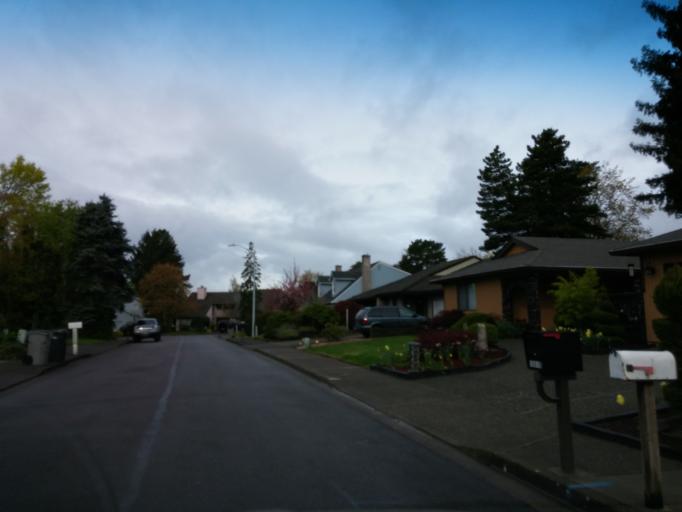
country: US
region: Oregon
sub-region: Washington County
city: Oak Hills
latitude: 45.5352
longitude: -122.8388
